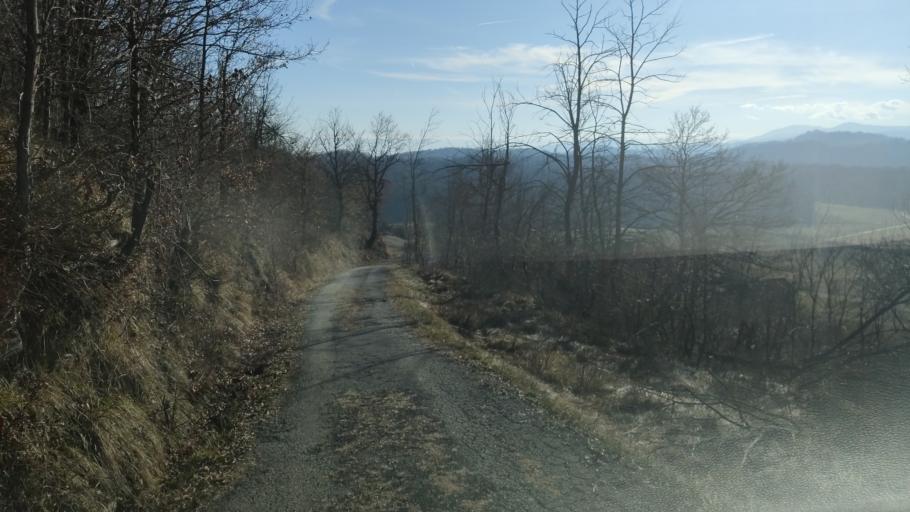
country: IT
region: Piedmont
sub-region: Provincia di Cuneo
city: Camerana
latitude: 44.4137
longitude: 8.1273
